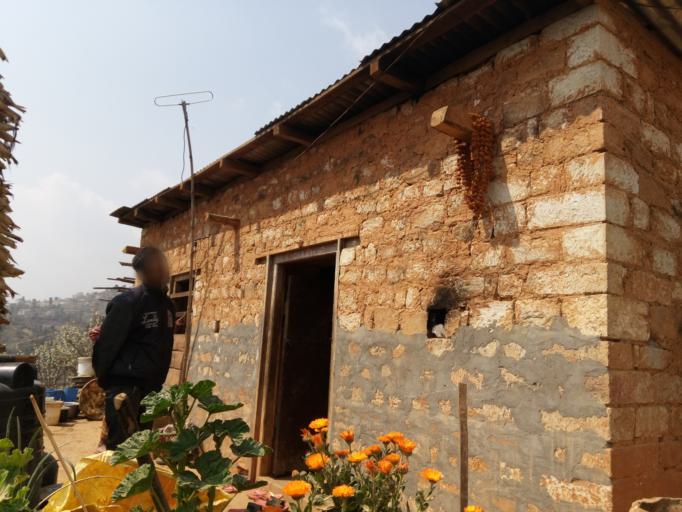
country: NP
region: Central Region
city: Kirtipur
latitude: 27.5843
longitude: 85.2643
